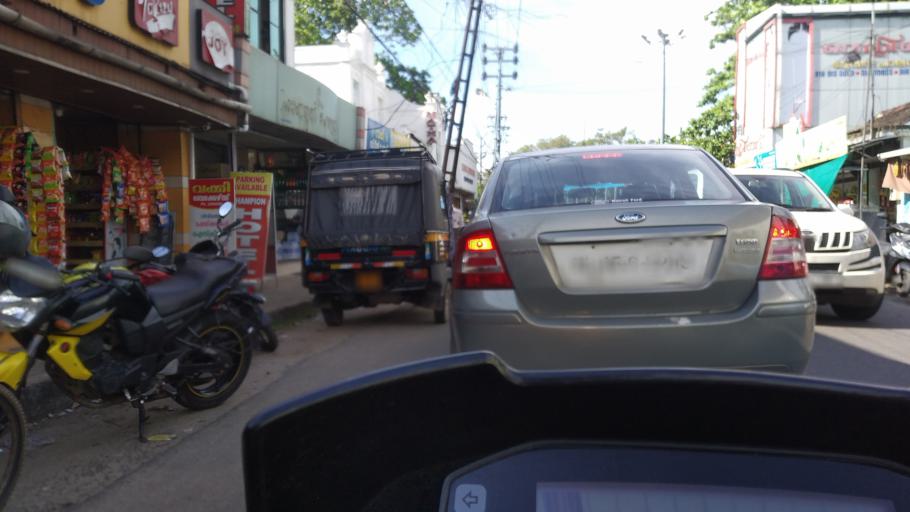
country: IN
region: Kerala
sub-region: Ernakulam
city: Elur
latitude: 10.0469
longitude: 76.2173
